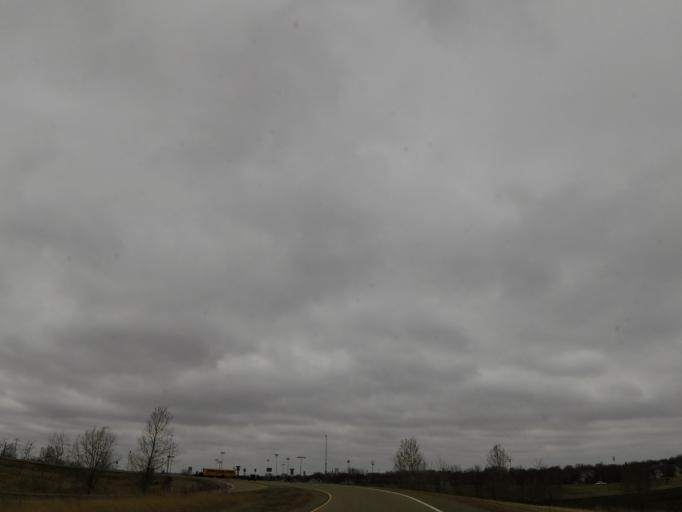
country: US
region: Minnesota
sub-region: Scott County
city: Shakopee
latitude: 44.7772
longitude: -93.5383
